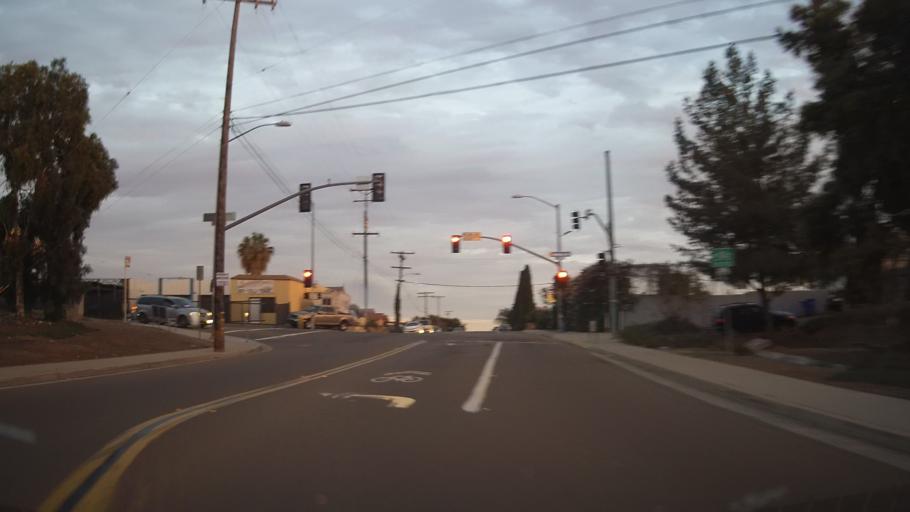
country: US
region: California
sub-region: San Diego County
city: National City
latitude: 32.7053
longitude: -117.1169
